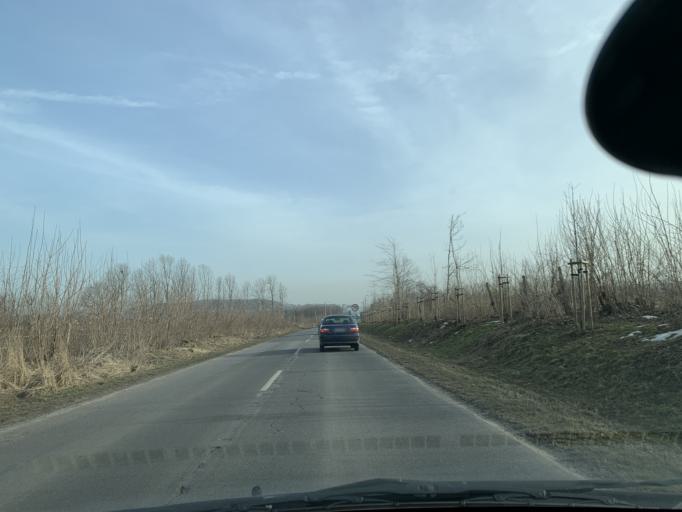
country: PL
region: Silesian Voivodeship
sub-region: Powiat tarnogorski
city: Radzionkow
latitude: 50.4106
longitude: 18.8941
